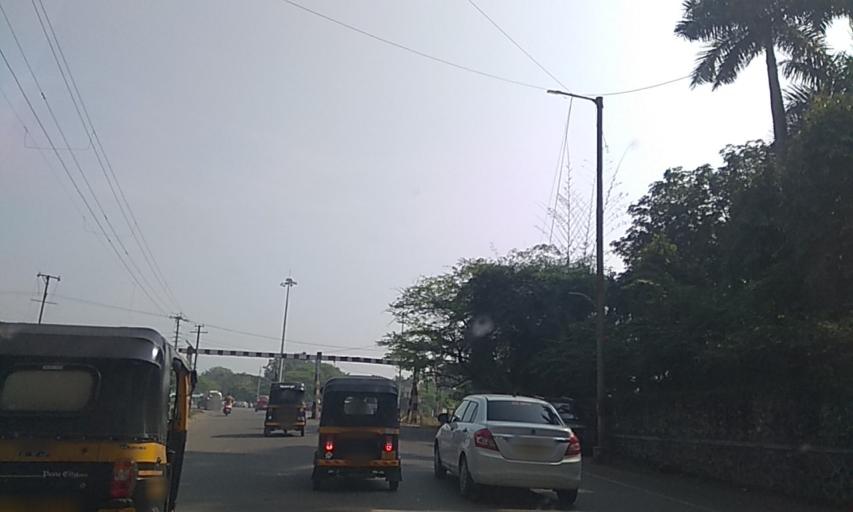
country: IN
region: Maharashtra
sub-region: Pune Division
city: Khadki
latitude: 18.5570
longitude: 73.8455
